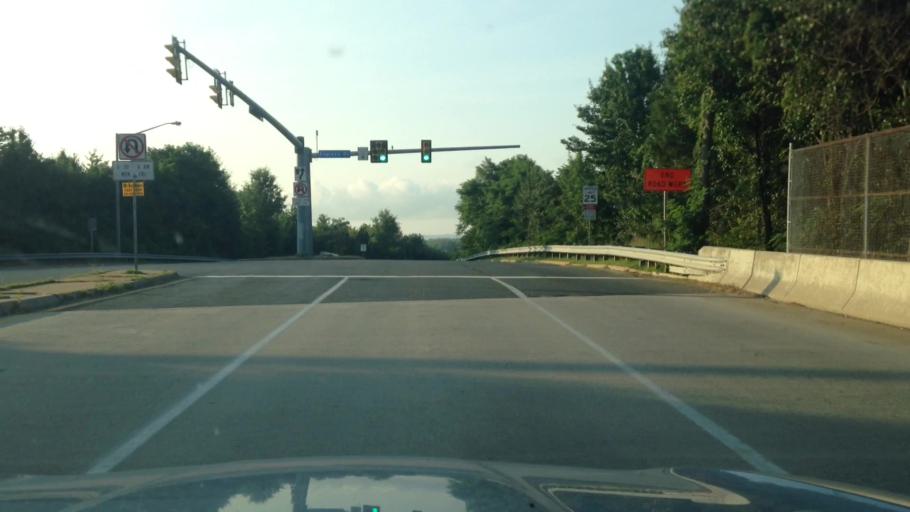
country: US
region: Virginia
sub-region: Prince William County
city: Woodbridge
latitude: 38.6575
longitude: -77.2489
